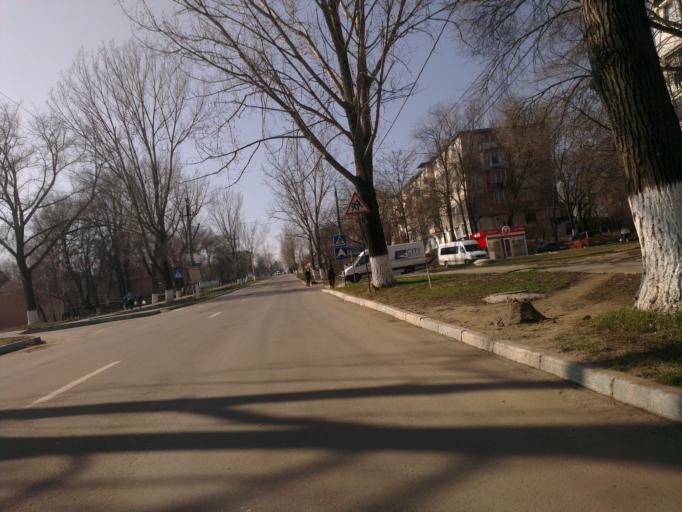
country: MD
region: Chisinau
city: Cricova
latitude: 47.1393
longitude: 28.8638
